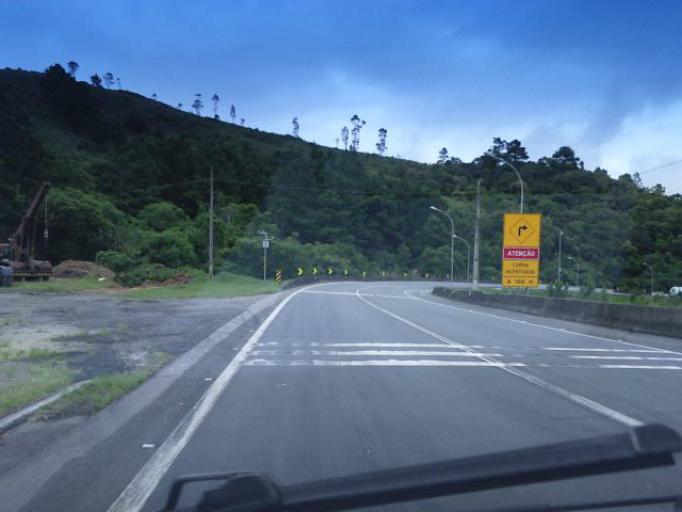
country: BR
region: Parana
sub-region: Campina Grande Do Sul
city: Campina Grande do Sul
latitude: -25.1134
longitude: -48.8472
